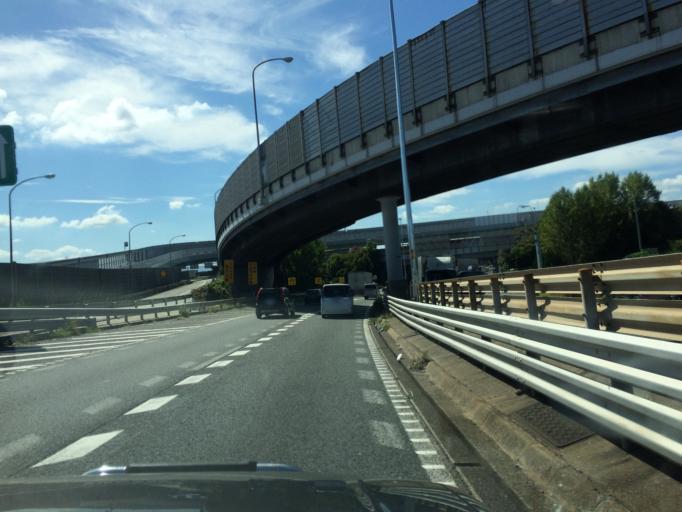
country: JP
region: Osaka
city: Yao
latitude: 34.5916
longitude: 135.5760
